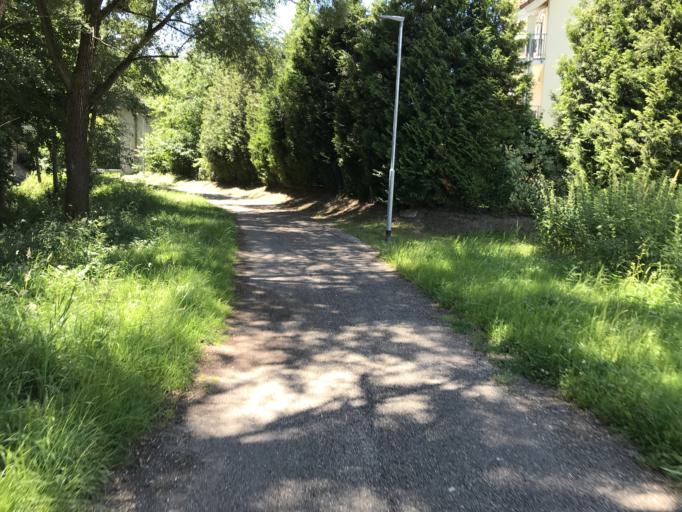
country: DE
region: Baden-Wuerttemberg
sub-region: Freiburg Region
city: Schopfheim
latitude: 47.6445
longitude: 7.8224
